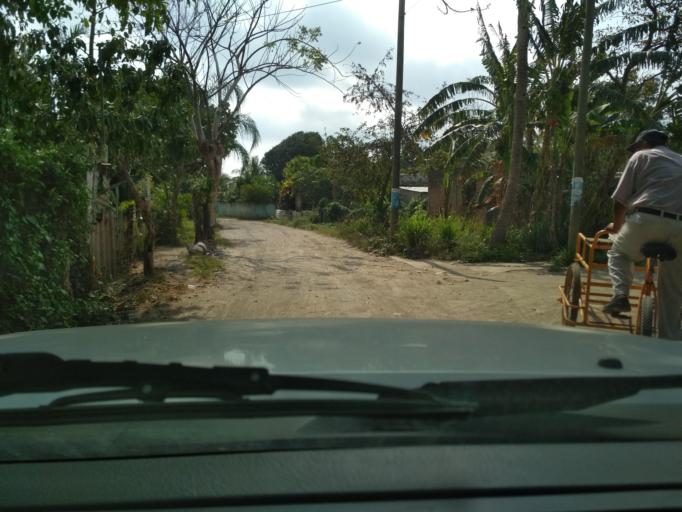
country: MX
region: Veracruz
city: El Tejar
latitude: 19.0807
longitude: -96.1645
